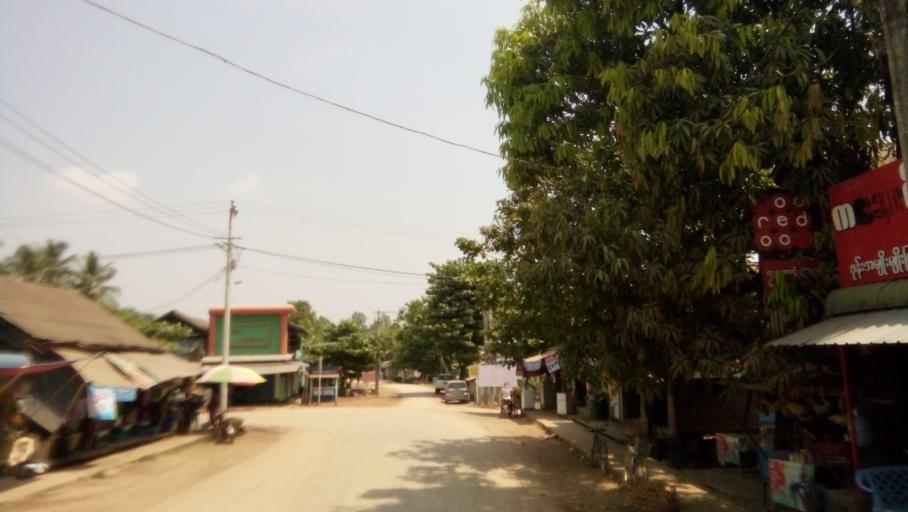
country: MM
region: Kayin
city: Hpa-an
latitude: 17.1231
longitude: 97.8195
